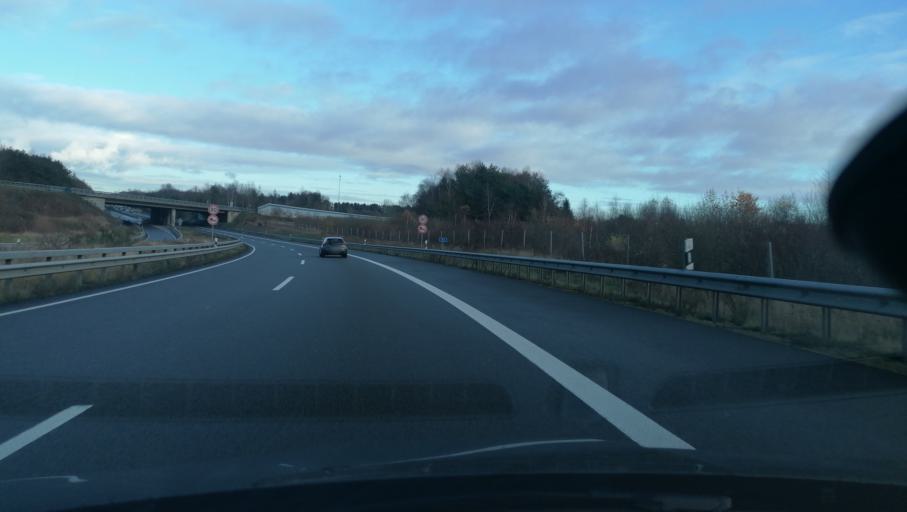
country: DE
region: Lower Saxony
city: Buchholz in der Nordheide
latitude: 53.3712
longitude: 9.8513
